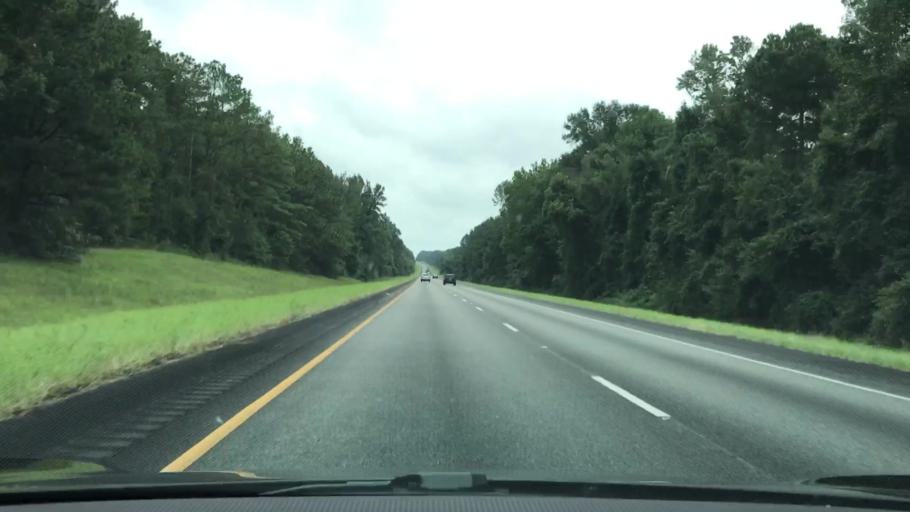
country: US
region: Alabama
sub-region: Elmore County
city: Tallassee
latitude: 32.4371
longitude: -85.8456
